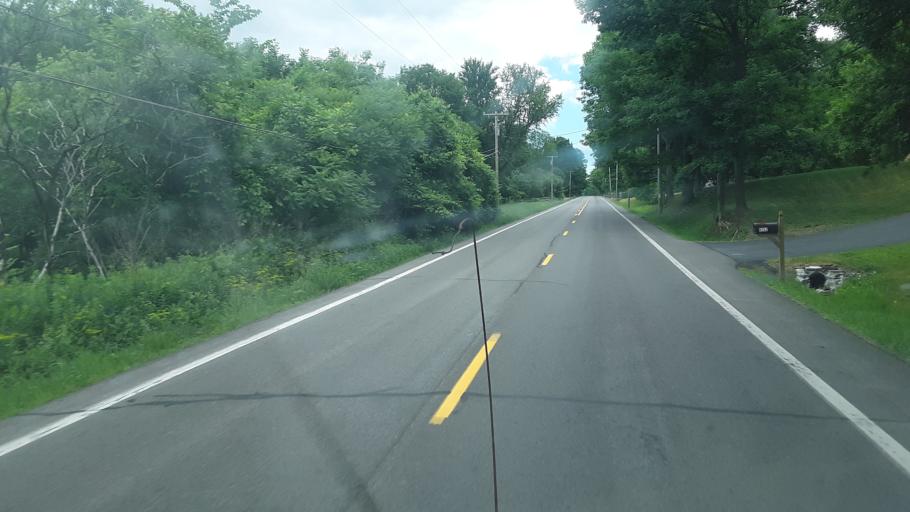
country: US
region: New York
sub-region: Oneida County
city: Rome
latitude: 43.3082
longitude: -75.4737
